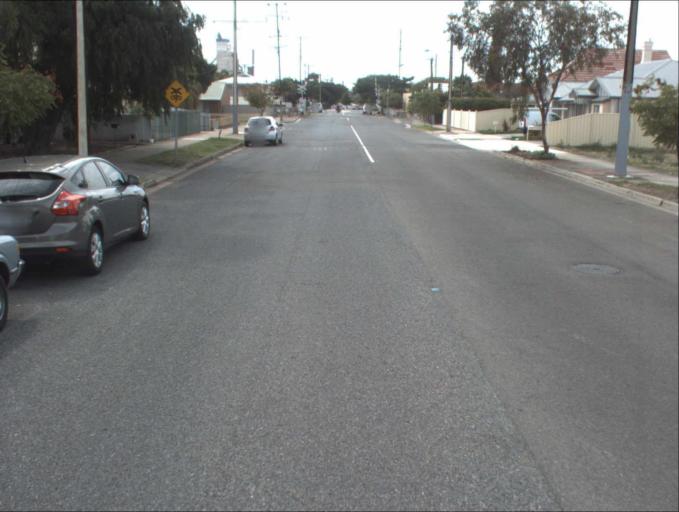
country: AU
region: South Australia
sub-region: Port Adelaide Enfield
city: Birkenhead
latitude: -34.8344
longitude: 138.4905
